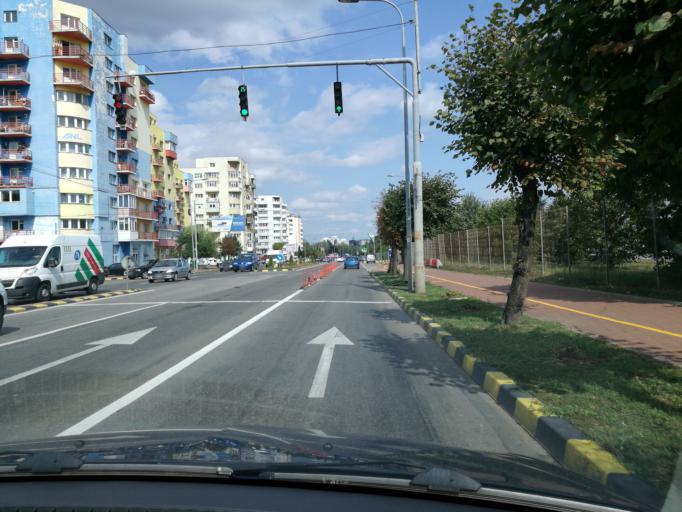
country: RO
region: Suceava
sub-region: Comuna Scheia
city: Scheia
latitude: 47.6352
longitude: 26.2337
